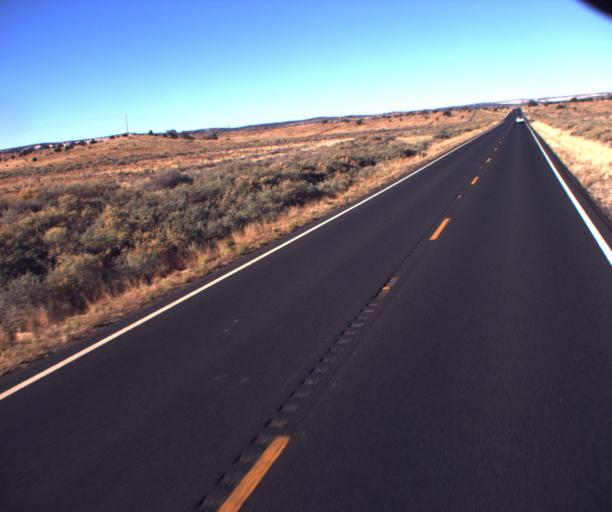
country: US
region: Arizona
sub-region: Apache County
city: Ganado
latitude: 35.7873
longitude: -109.6884
